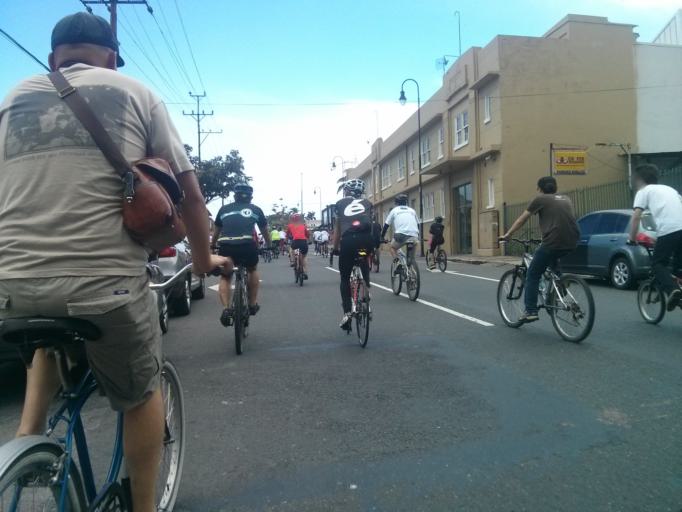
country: CR
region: San Jose
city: San Jose
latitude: 9.9336
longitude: -84.0681
